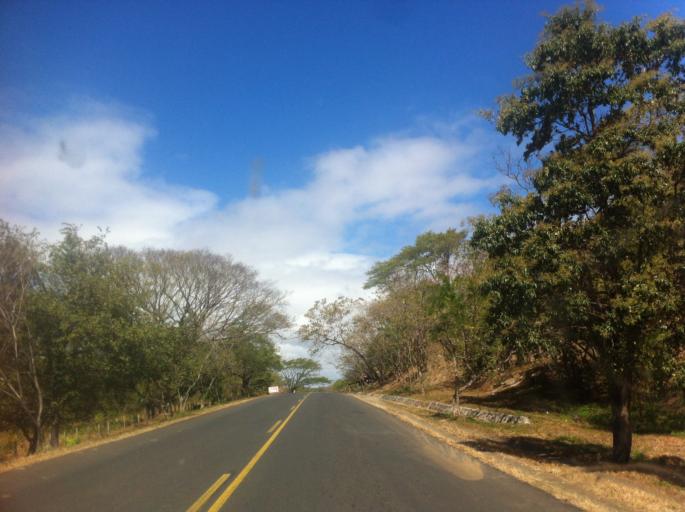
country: NI
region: Chontales
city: Acoyapa
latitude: 12.0112
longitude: -85.2423
